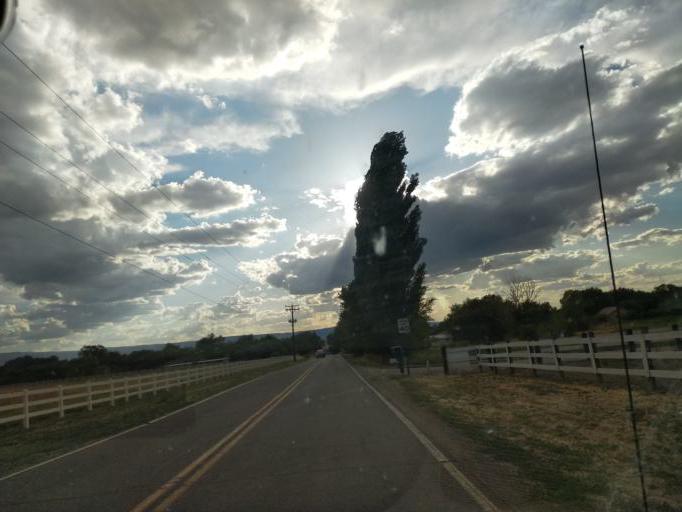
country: US
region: Colorado
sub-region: Mesa County
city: Clifton
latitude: 39.0560
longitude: -108.4223
